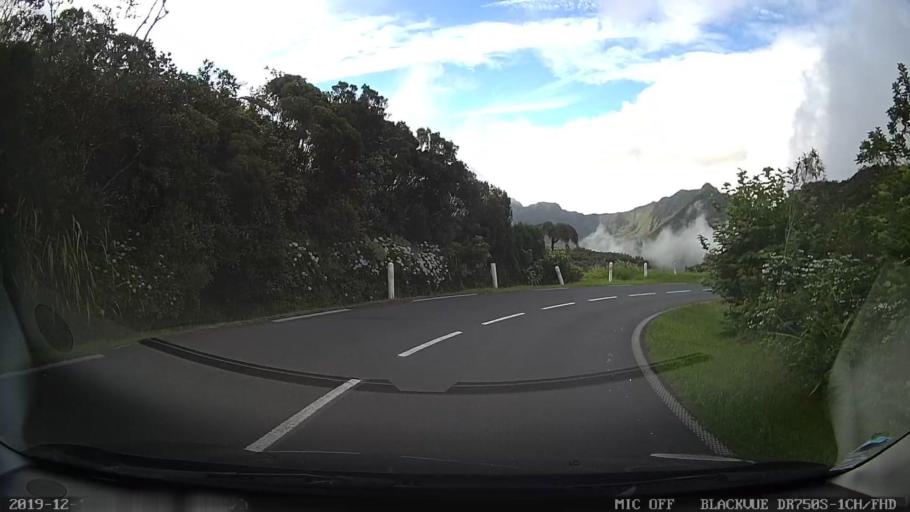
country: RE
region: Reunion
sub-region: Reunion
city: Cilaos
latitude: -21.1583
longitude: 55.5966
